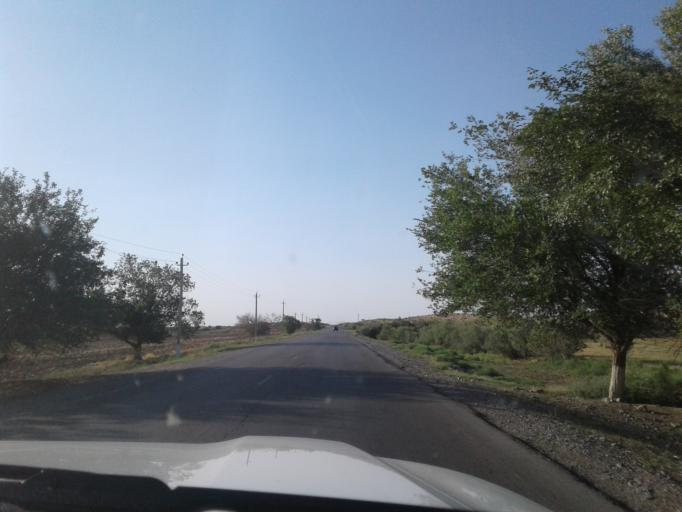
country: TM
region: Mary
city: Yoloeten
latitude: 37.2258
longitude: 62.3748
